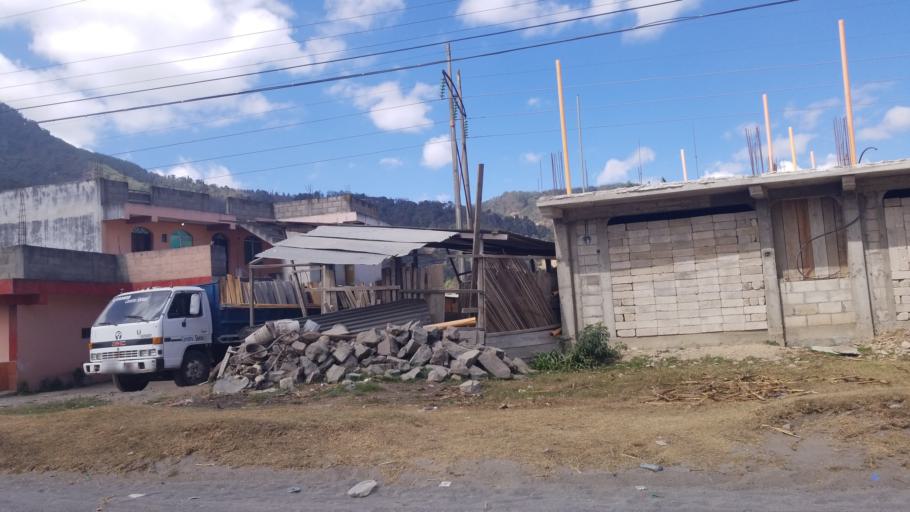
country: GT
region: Quetzaltenango
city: Almolonga
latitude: 14.7868
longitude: -91.5366
